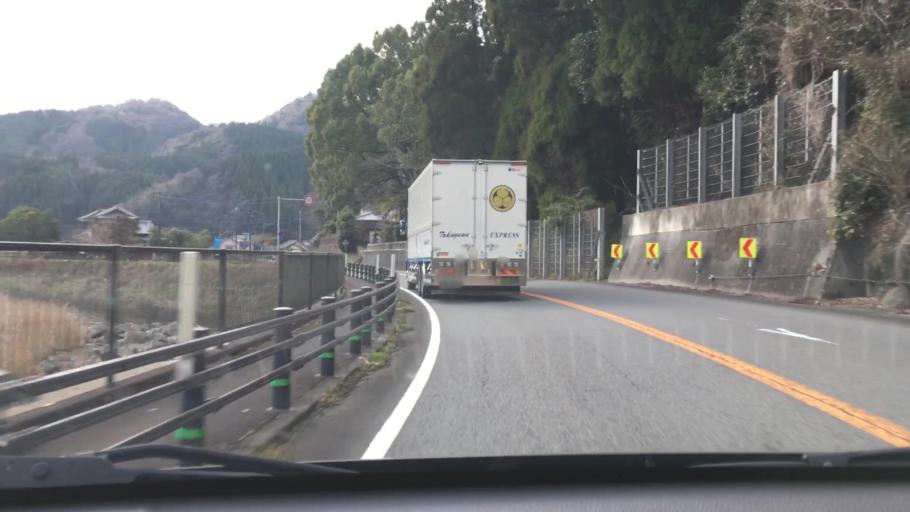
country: JP
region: Oita
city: Usuki
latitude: 33.0084
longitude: 131.7115
